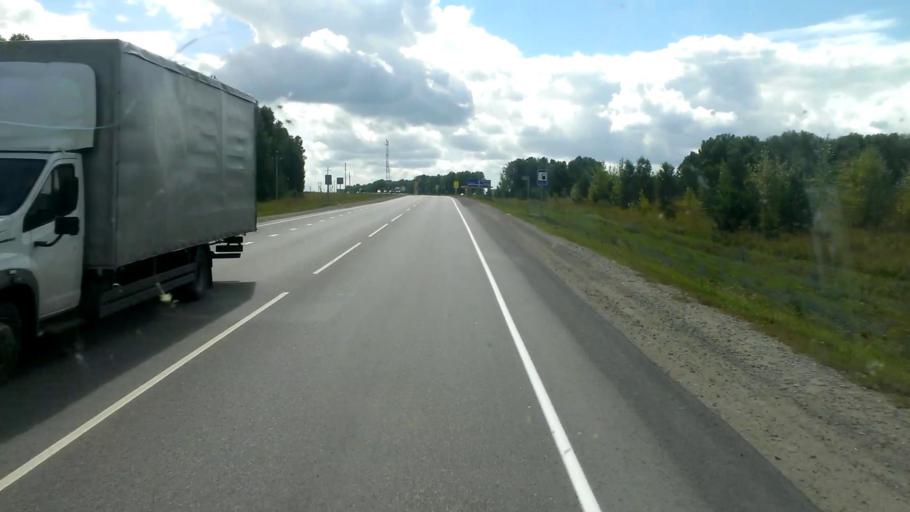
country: RU
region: Altai Krai
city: Troitskoye
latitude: 52.9728
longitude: 84.7477
